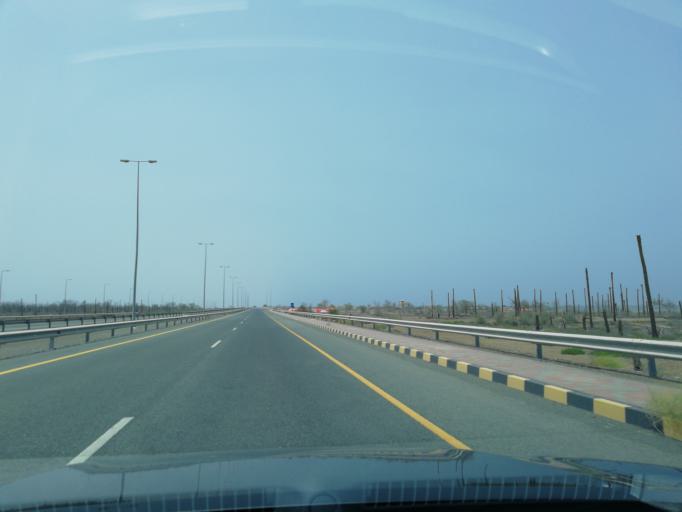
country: OM
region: Al Batinah
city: Shinas
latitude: 24.6511
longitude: 56.5153
